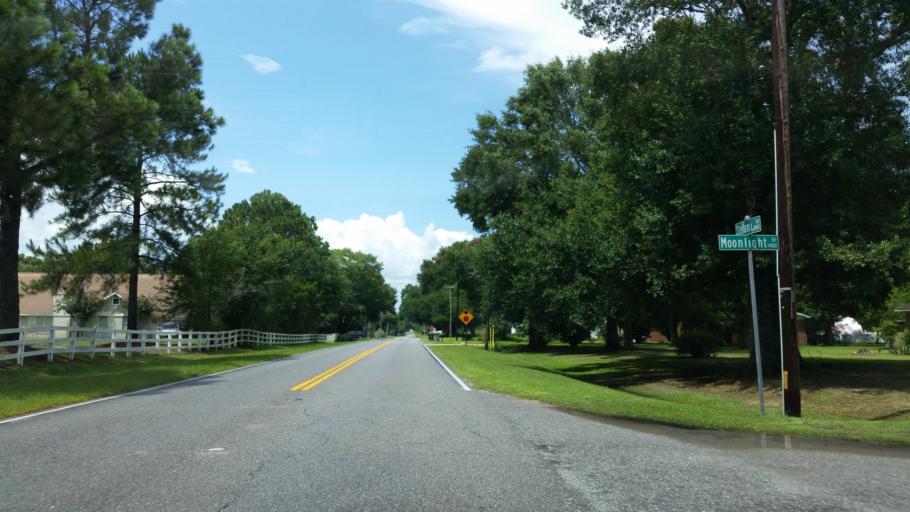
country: US
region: Florida
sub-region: Escambia County
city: Ensley
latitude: 30.5397
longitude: -87.3004
